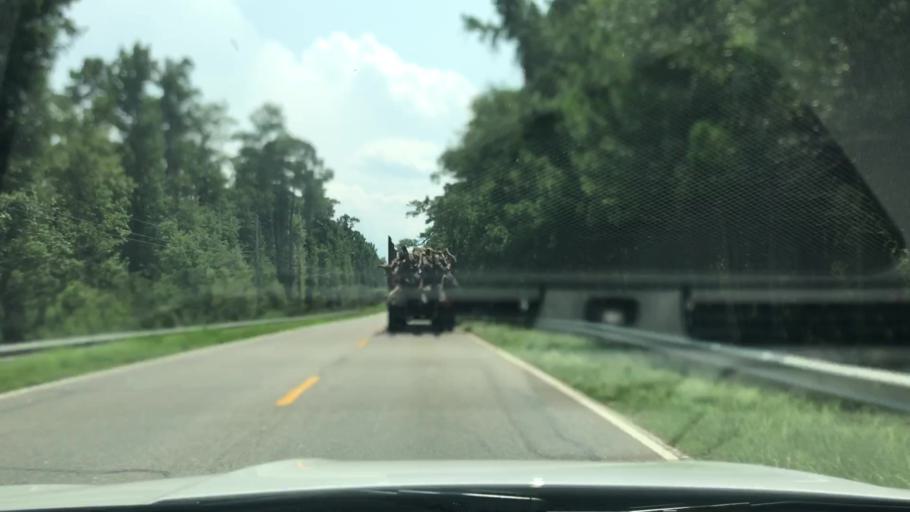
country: US
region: South Carolina
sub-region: Georgetown County
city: Georgetown
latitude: 33.4689
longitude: -79.2797
